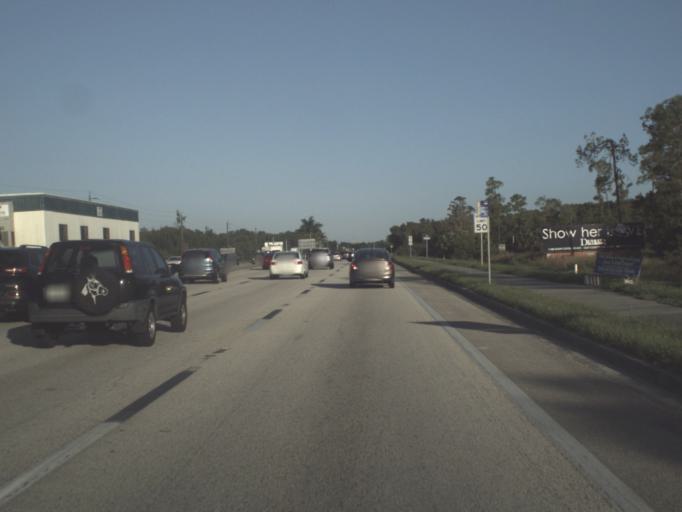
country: US
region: Florida
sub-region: Lee County
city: San Carlos Park
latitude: 26.4960
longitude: -81.8499
